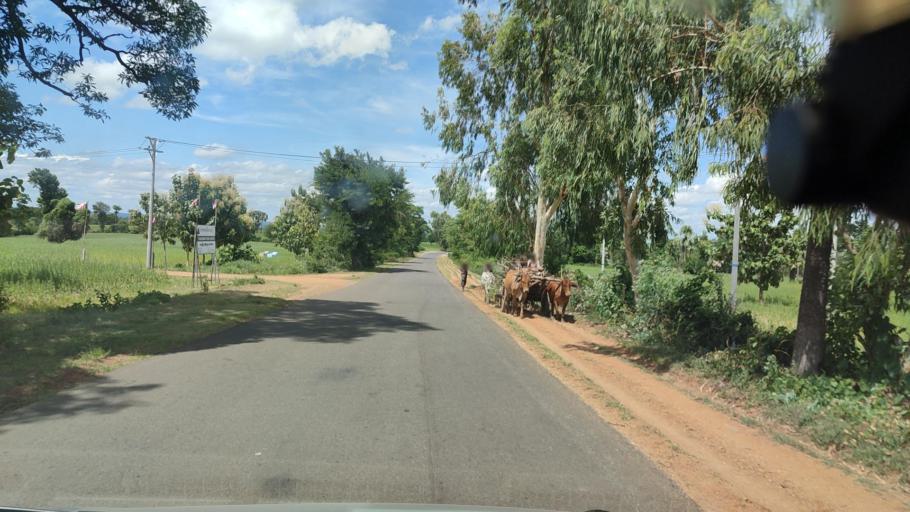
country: MM
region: Magway
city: Magway
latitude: 20.1933
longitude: 95.0975
